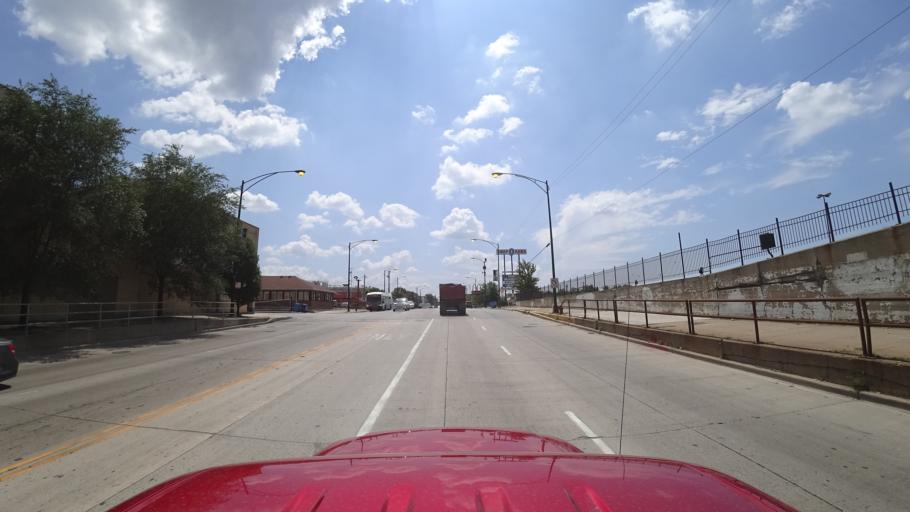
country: US
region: Illinois
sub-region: Cook County
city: Chicago
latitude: 41.8196
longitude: -87.6653
